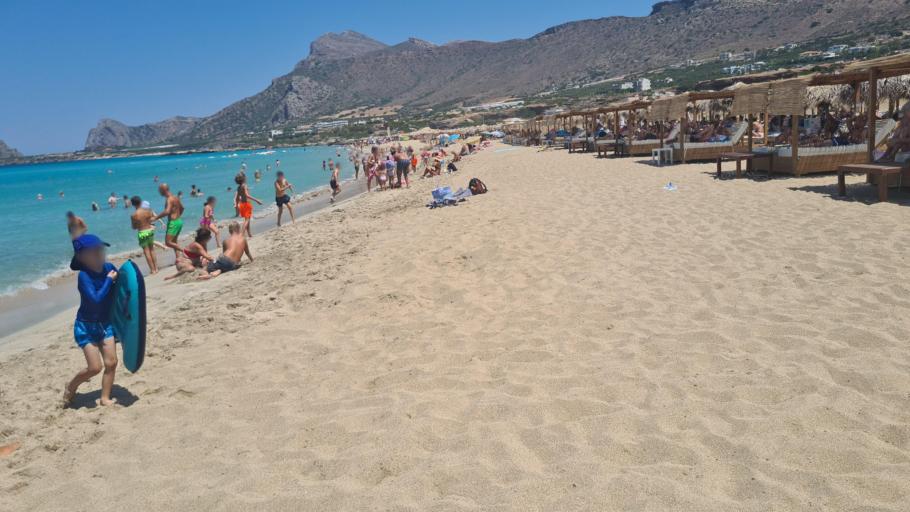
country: GR
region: Crete
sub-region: Nomos Chanias
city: Platanos
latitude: 35.4921
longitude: 23.5795
